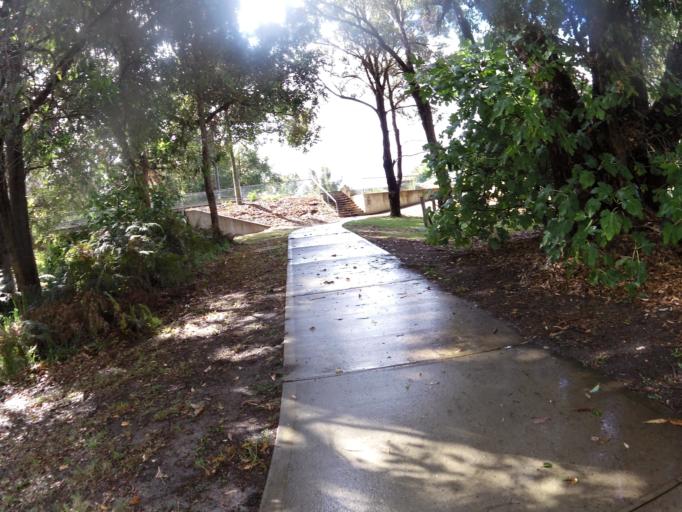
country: AU
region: Western Australia
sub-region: Donnybrook-Balingup
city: Donnybrook
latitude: -33.5717
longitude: 115.8260
